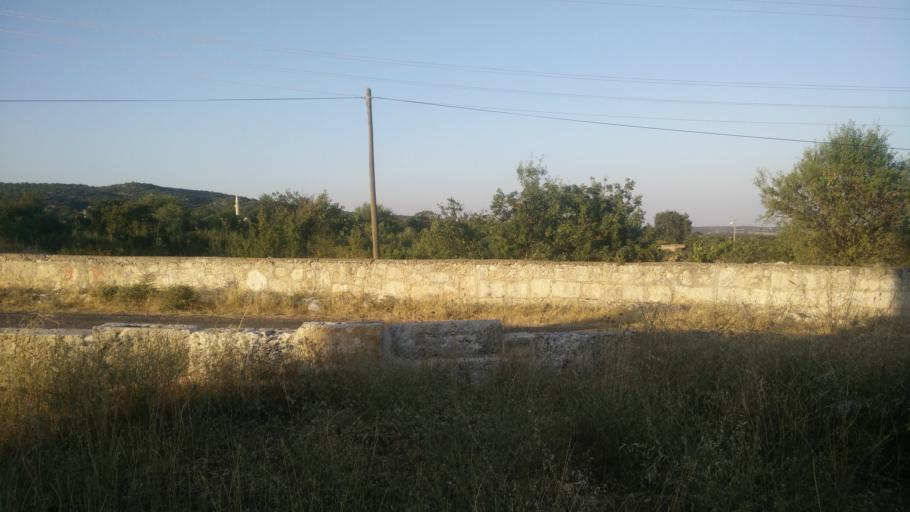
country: TR
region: Mersin
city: Silifke
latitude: 36.5749
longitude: 34.0332
